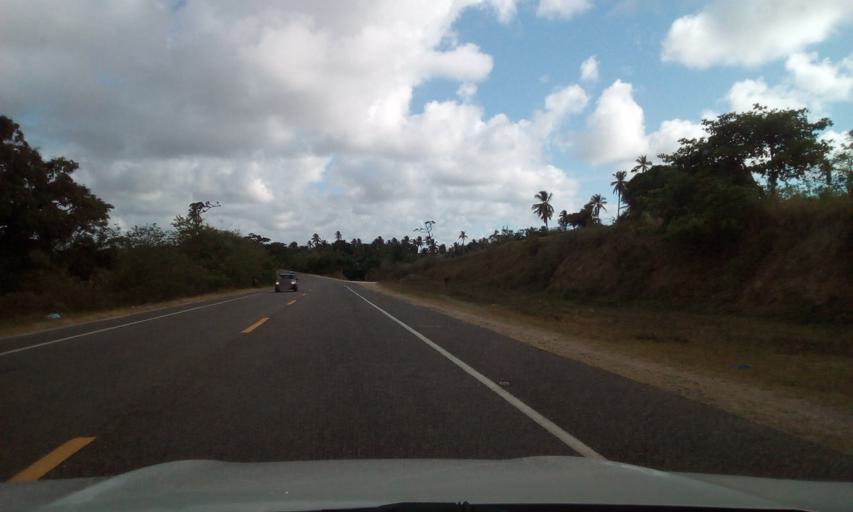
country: BR
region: Bahia
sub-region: Conde
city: Conde
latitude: -11.8011
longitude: -37.6281
